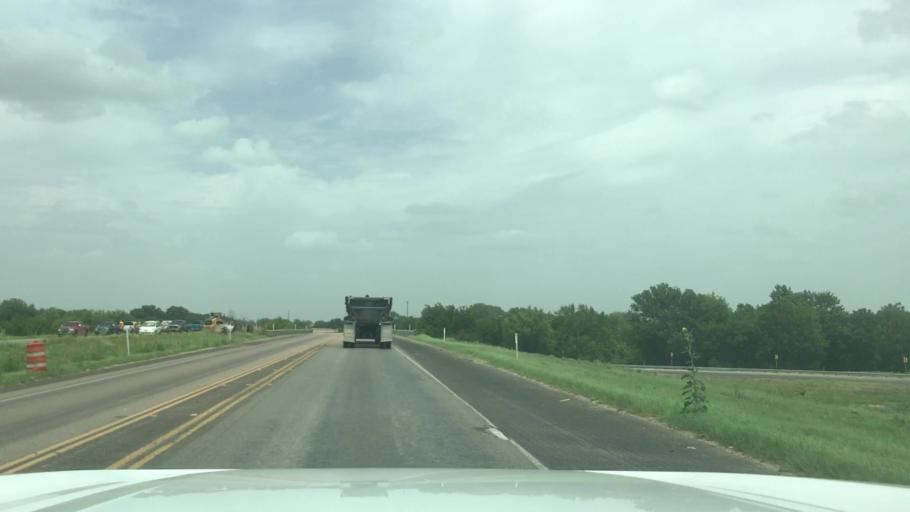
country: US
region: Texas
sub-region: McLennan County
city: Beverly
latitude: 31.5338
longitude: -97.0755
